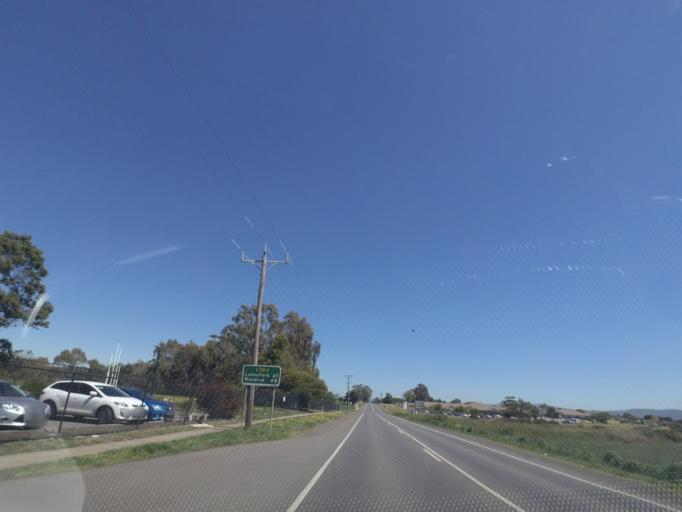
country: AU
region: Victoria
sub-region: Whittlesea
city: Whittlesea
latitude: -37.2956
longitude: 144.9472
